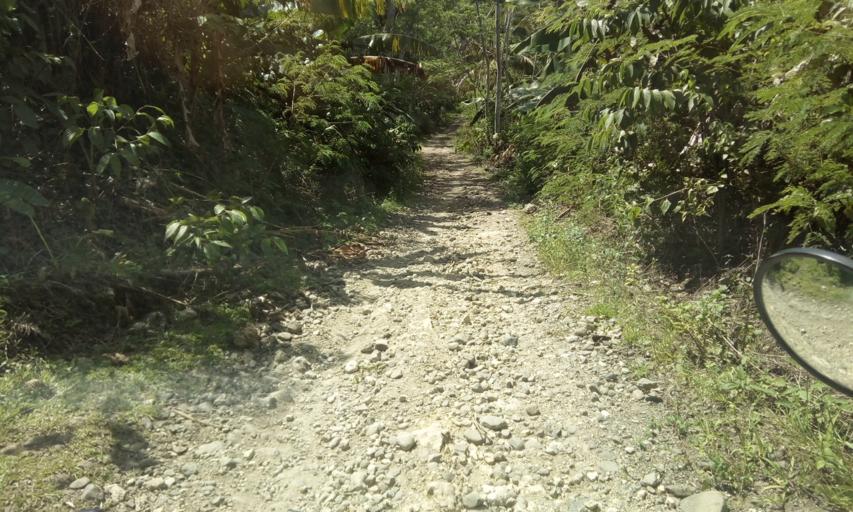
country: PH
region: Caraga
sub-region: Province of Agusan del Sur
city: Santa Josefa
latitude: 7.9543
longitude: 125.9868
